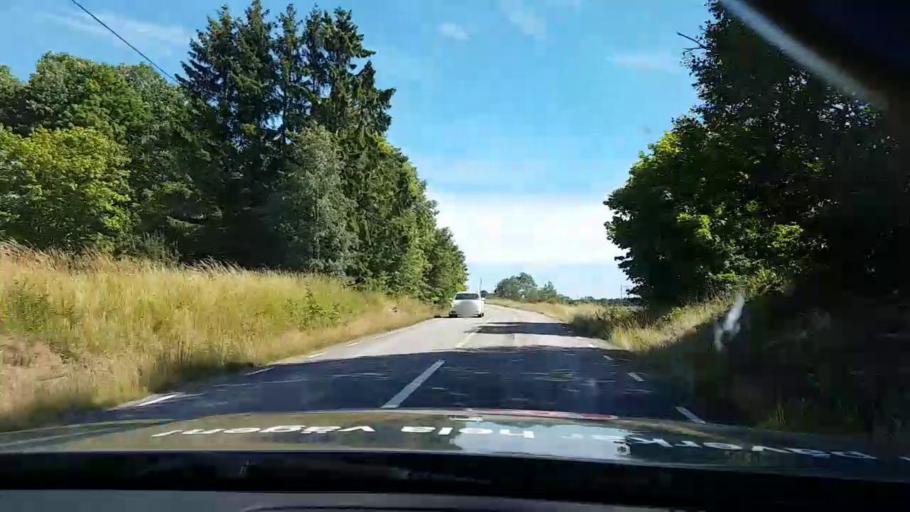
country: SE
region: Kalmar
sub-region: Vasterviks Kommun
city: Forserum
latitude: 57.9362
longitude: 16.5031
